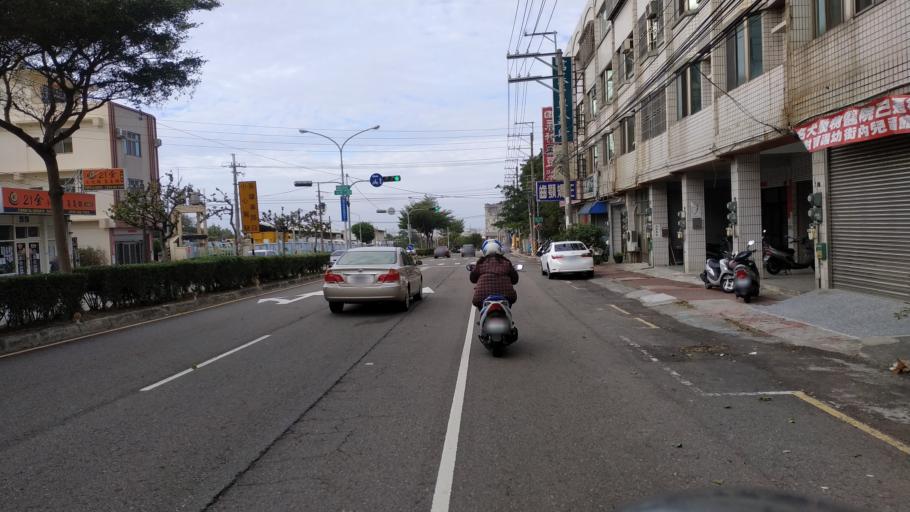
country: TW
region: Taiwan
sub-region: Taichung City
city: Taichung
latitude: 24.2307
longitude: 120.5663
